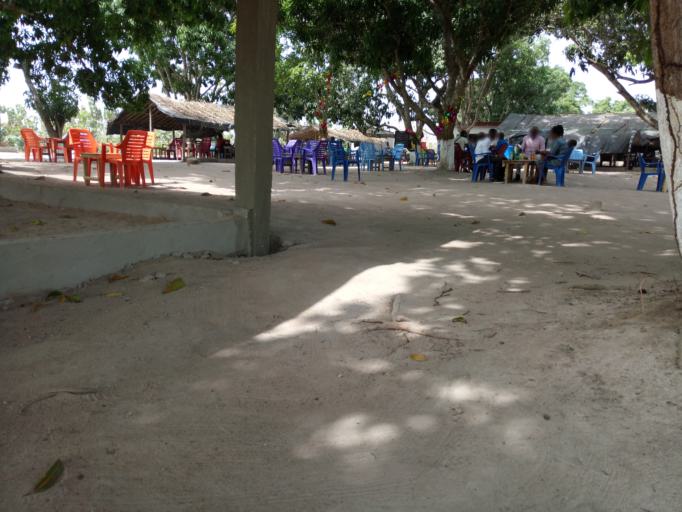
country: CI
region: Vallee du Bandama
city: Bouake
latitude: 7.6860
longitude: -5.1097
